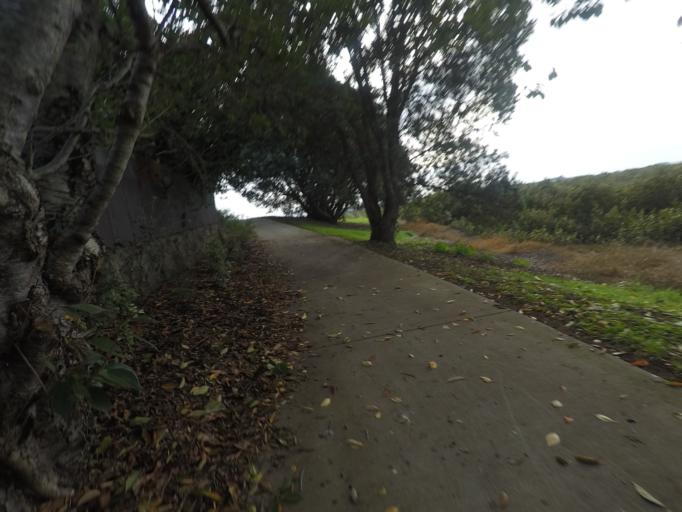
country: NZ
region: Auckland
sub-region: Auckland
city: Mangere
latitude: -36.9444
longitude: 174.7982
